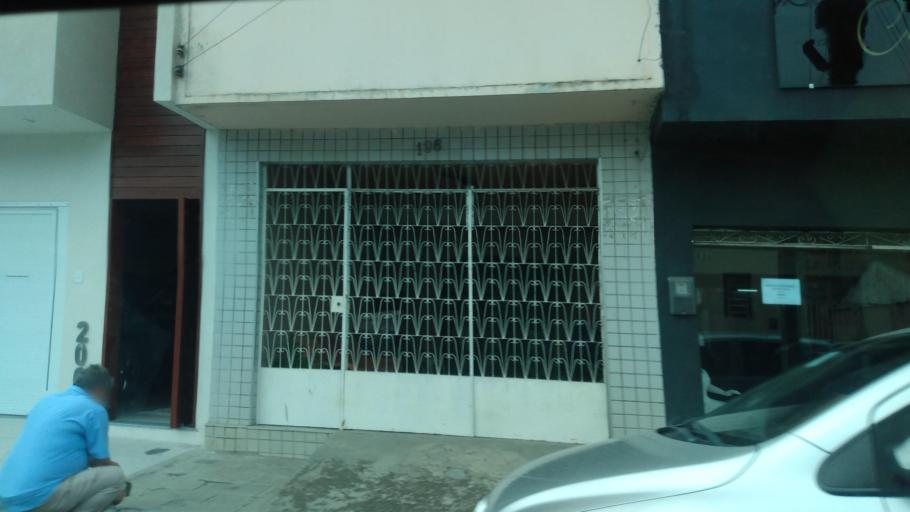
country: BR
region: Pernambuco
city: Garanhuns
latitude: -8.8858
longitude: -36.4883
